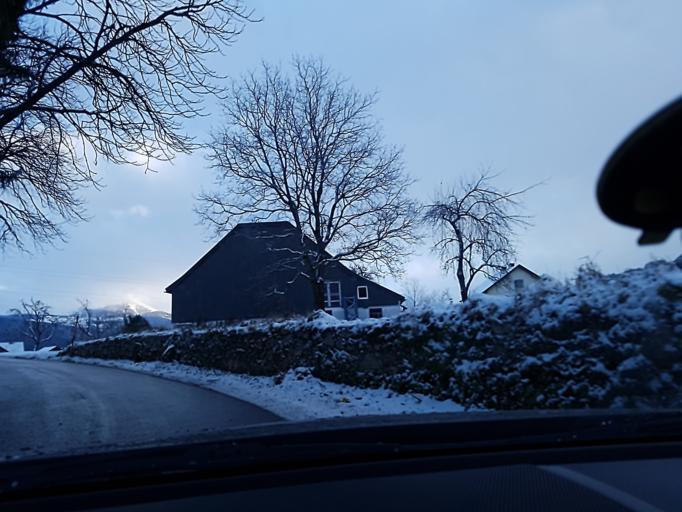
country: AT
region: Salzburg
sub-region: Politischer Bezirk Salzburg-Umgebung
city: Grodig
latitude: 47.7215
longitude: 13.0563
